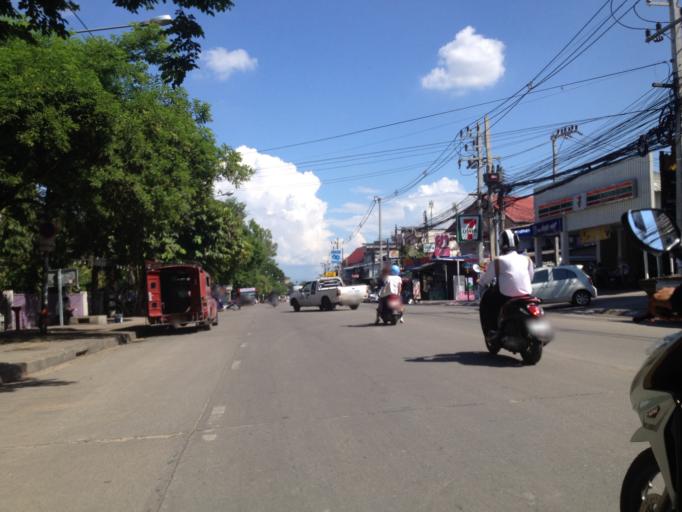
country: TH
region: Chiang Mai
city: Chiang Mai
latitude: 18.7924
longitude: 98.9564
